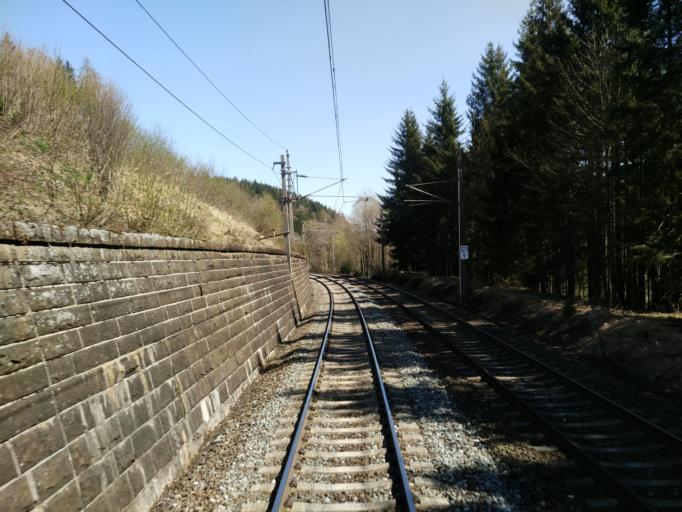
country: AT
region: Salzburg
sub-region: Politischer Bezirk Zell am See
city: Leogang
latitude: 47.4440
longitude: 12.7013
